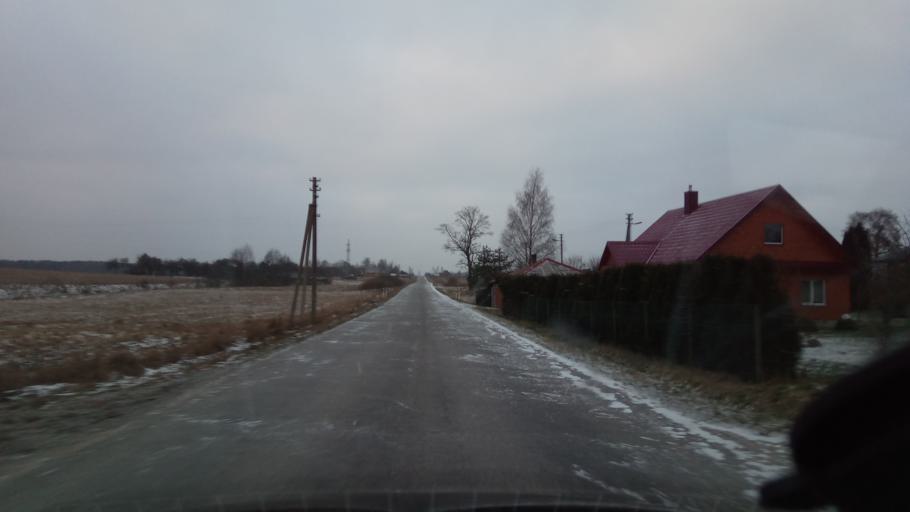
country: LT
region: Alytaus apskritis
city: Varena
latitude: 54.1170
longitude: 24.7529
